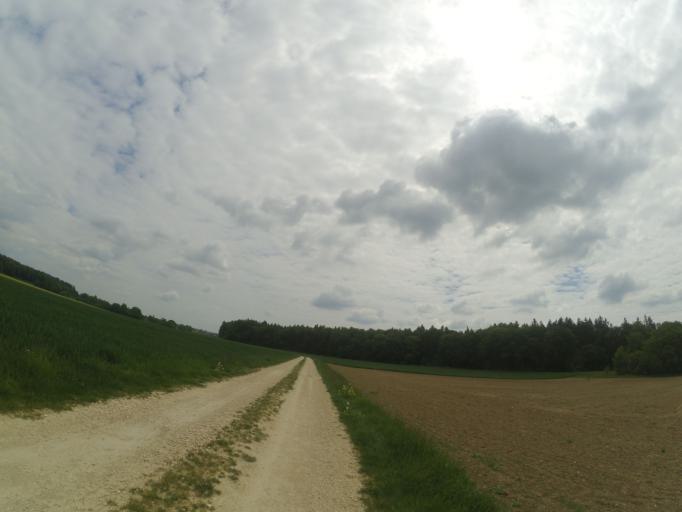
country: DE
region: Baden-Wuerttemberg
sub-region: Tuebingen Region
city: Blaubeuren
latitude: 48.4252
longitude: 9.8343
